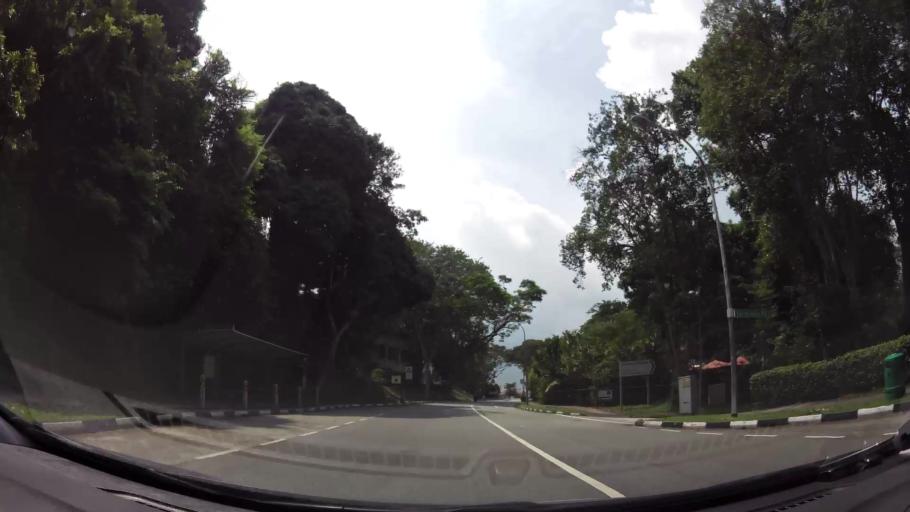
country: MY
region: Johor
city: Kampung Pasir Gudang Baru
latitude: 1.3892
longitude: 103.9785
